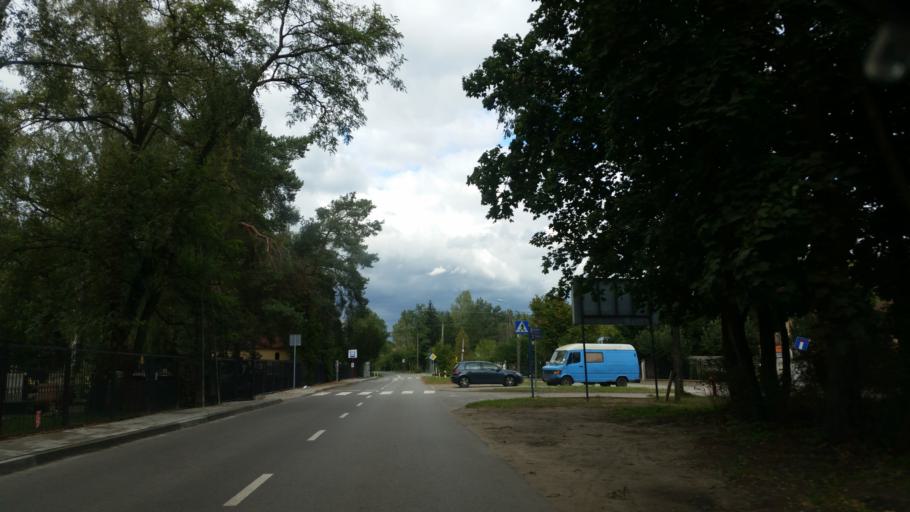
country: PL
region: Masovian Voivodeship
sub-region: Powiat piaseczynski
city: Konstancin-Jeziorna
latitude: 52.0669
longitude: 21.0995
